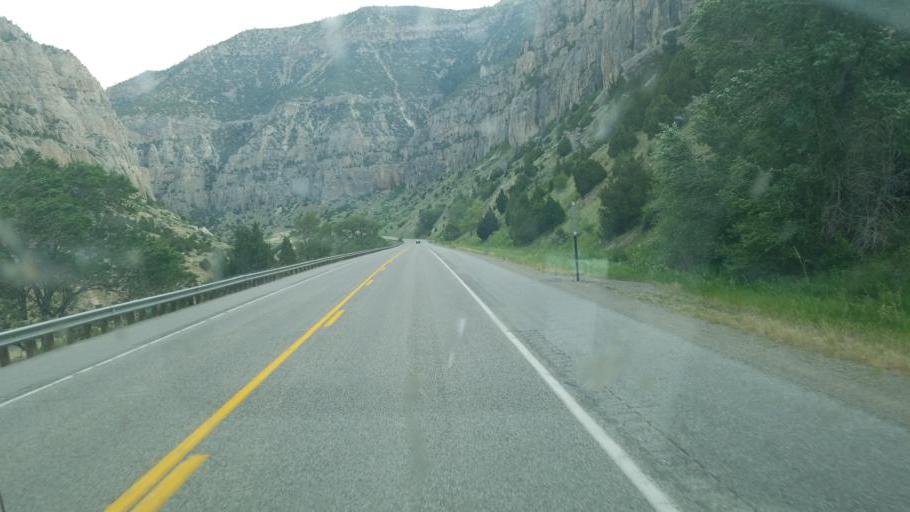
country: US
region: Wyoming
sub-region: Hot Springs County
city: Thermopolis
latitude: 43.5191
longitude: -108.1807
